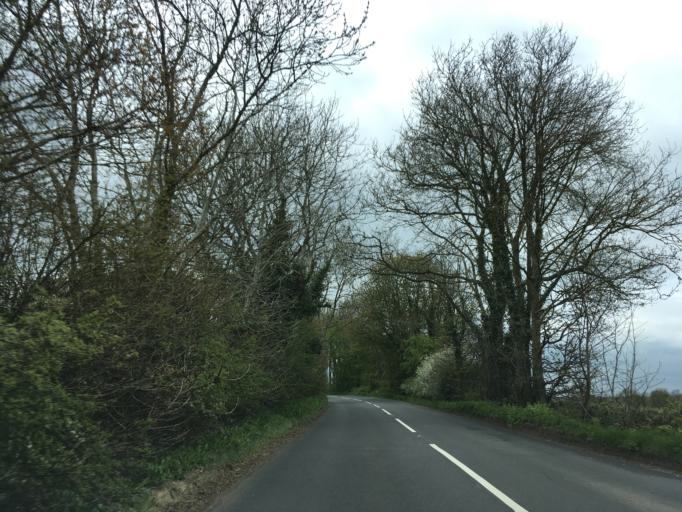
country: GB
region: England
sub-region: Gloucestershire
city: Nailsworth
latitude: 51.6895
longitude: -2.2784
